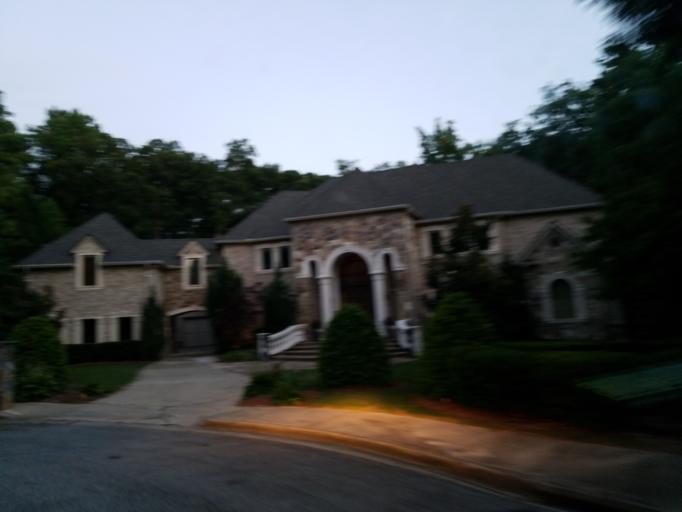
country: US
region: Georgia
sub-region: Cobb County
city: Vinings
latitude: 33.8694
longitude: -84.4247
